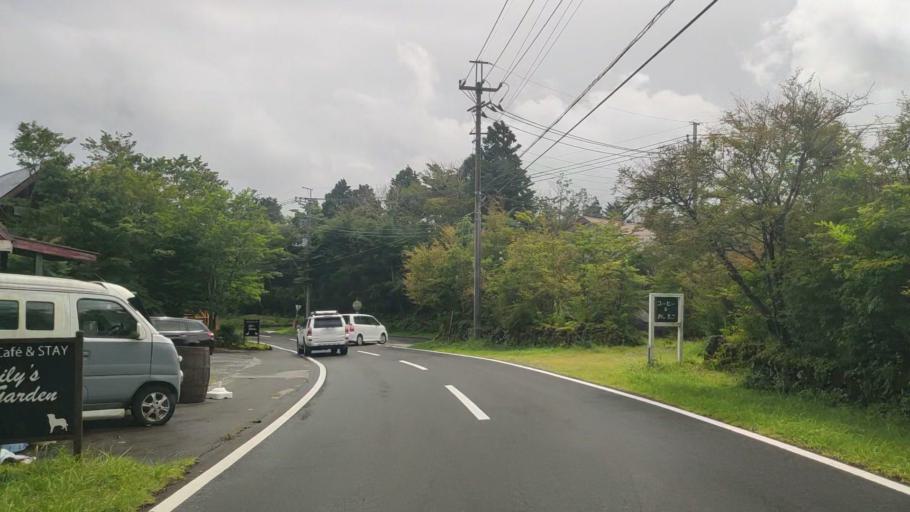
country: JP
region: Shizuoka
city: Gotemba
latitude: 35.2700
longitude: 138.7977
